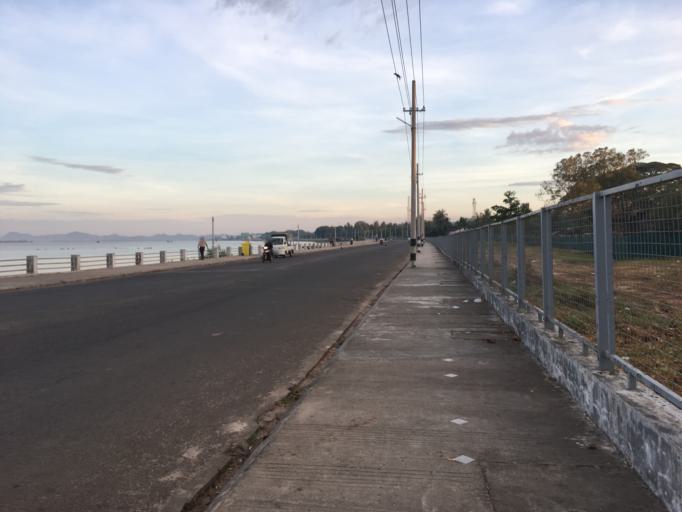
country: MM
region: Mon
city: Mawlamyine
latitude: 16.4527
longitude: 97.6230
